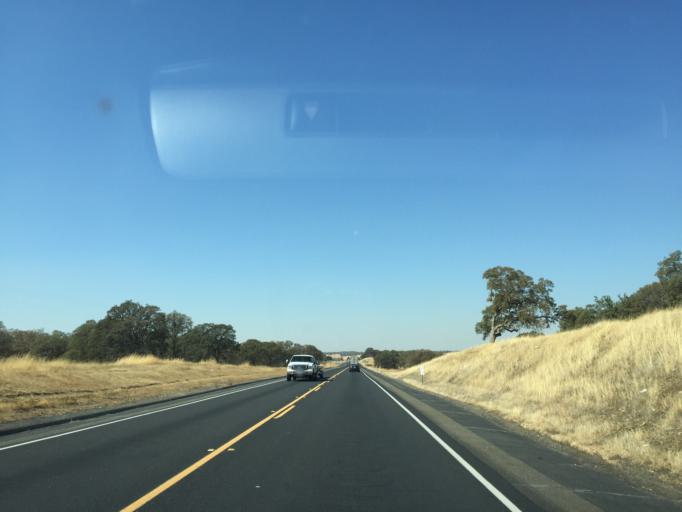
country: US
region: California
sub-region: Tuolumne County
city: Jamestown
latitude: 37.8413
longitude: -120.5193
